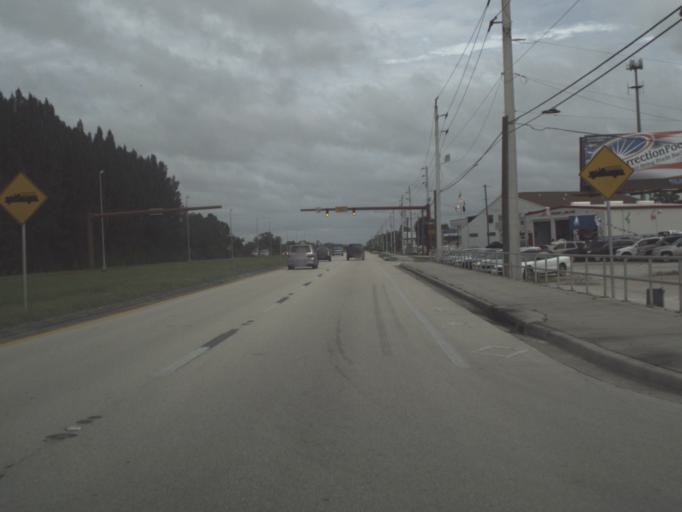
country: US
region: Florida
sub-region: Sarasota County
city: North Port
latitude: 26.9651
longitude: -82.2109
